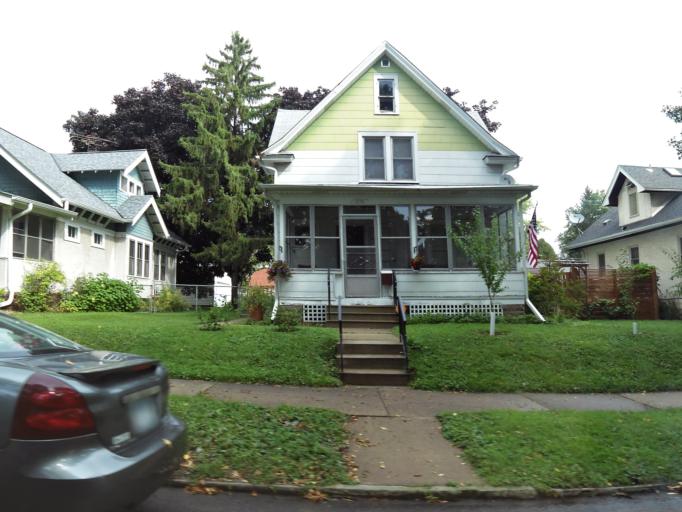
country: US
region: Minnesota
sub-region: Dakota County
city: Mendota Heights
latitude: 44.9270
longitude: -93.1531
